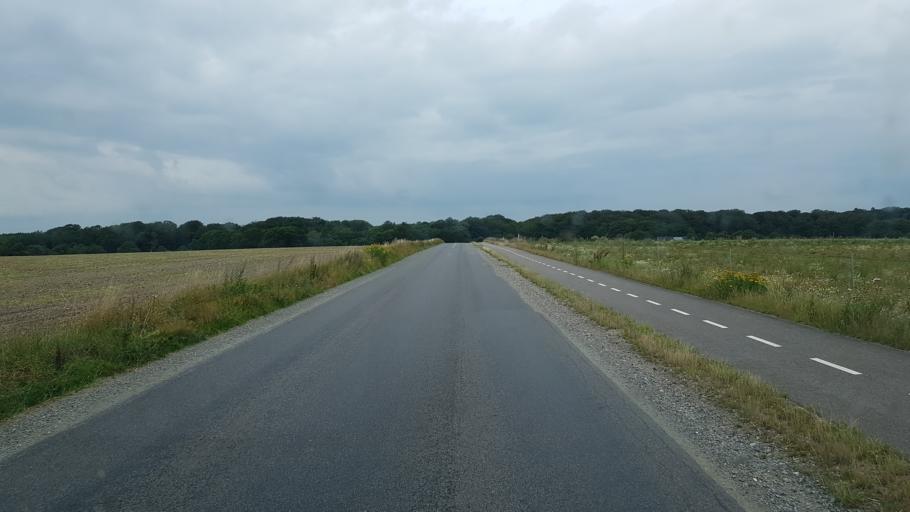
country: DK
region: South Denmark
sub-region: Varde Kommune
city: Olgod
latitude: 55.6997
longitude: 8.6467
